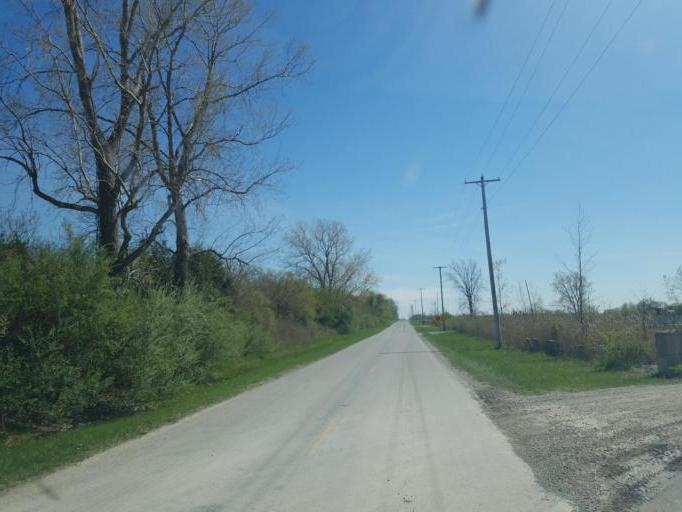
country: US
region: Ohio
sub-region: Huron County
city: Bellevue
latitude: 41.3375
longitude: -82.7937
